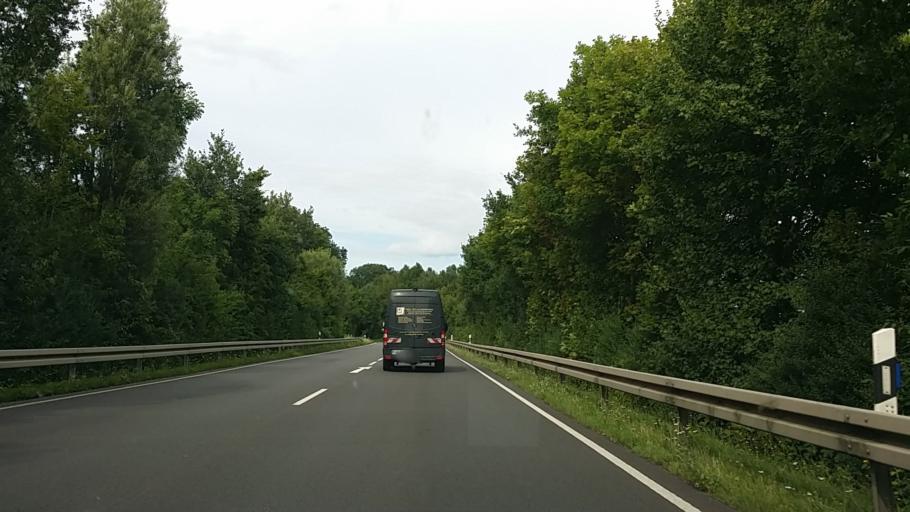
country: DE
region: Saxony-Anhalt
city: Osterburg
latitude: 52.8024
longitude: 11.7468
